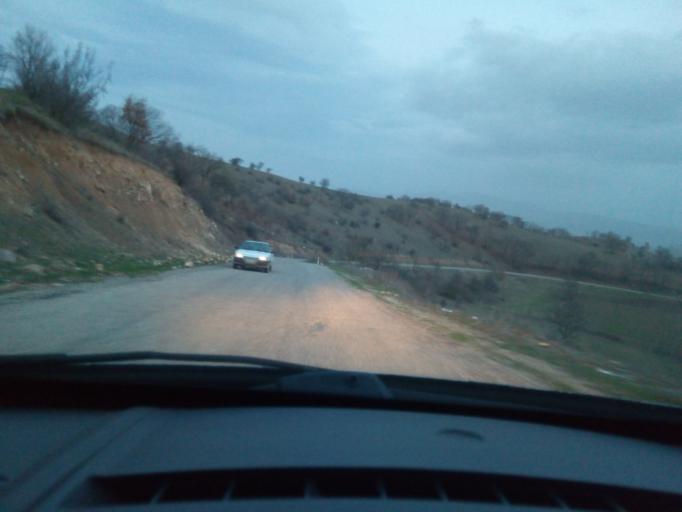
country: TR
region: Balikesir
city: Susurluk
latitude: 39.9149
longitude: 28.0979
